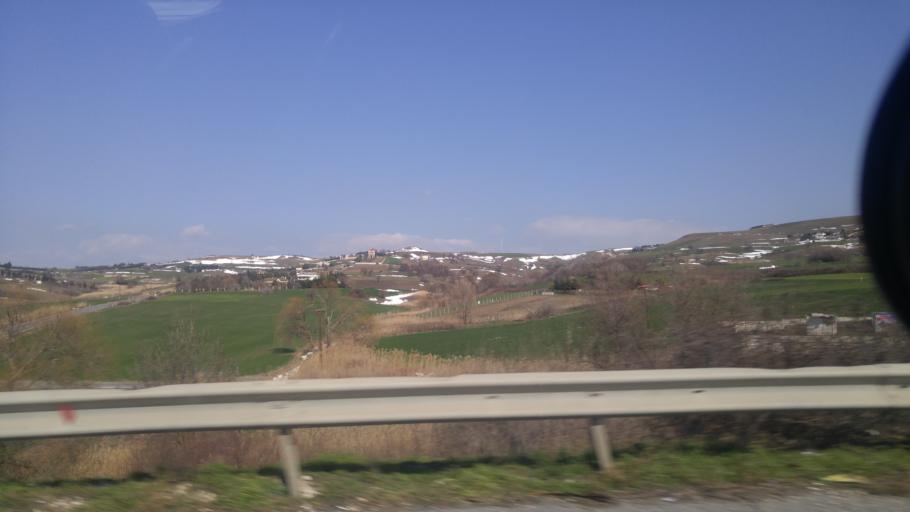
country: TR
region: Istanbul
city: Celaliye
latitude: 41.0642
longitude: 28.4047
